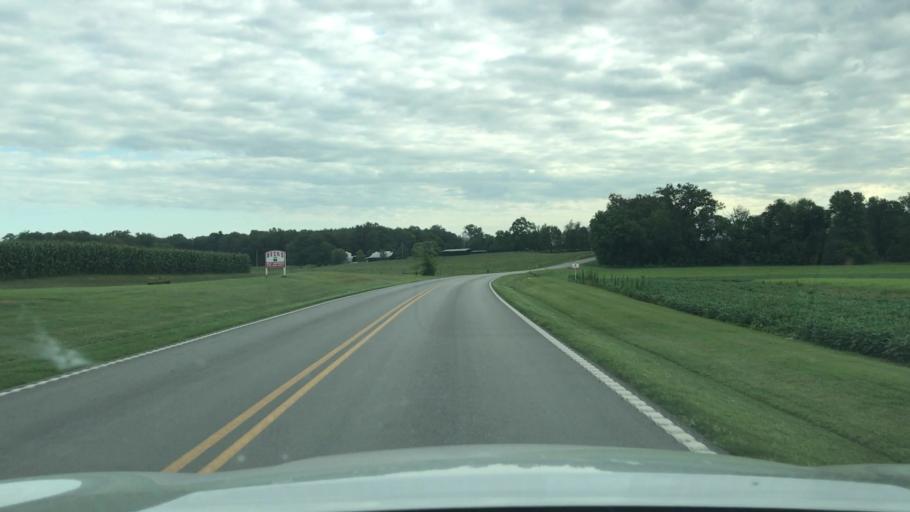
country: US
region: Kentucky
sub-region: Todd County
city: Elkton
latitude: 36.7335
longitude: -87.1888
